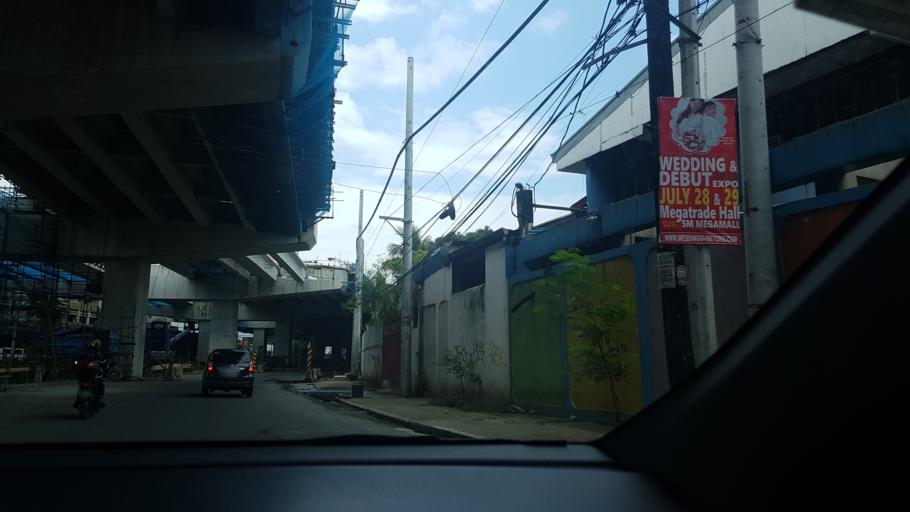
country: PH
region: Calabarzon
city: Del Monte
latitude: 14.6375
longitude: 121.0084
